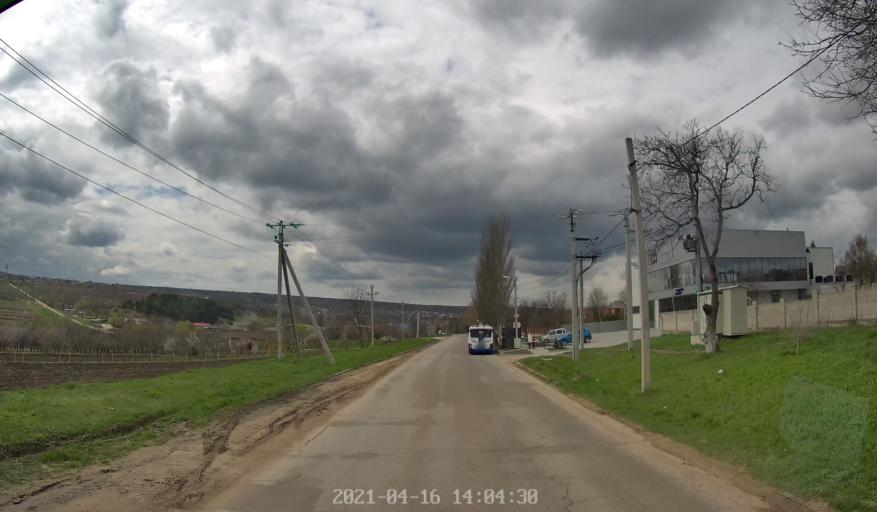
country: MD
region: Chisinau
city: Vatra
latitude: 47.0718
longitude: 28.6998
